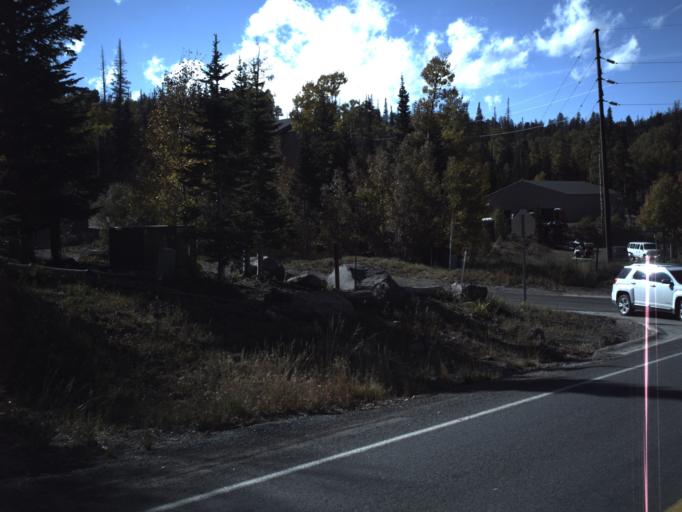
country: US
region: Utah
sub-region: Iron County
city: Parowan
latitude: 37.7058
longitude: -112.8495
